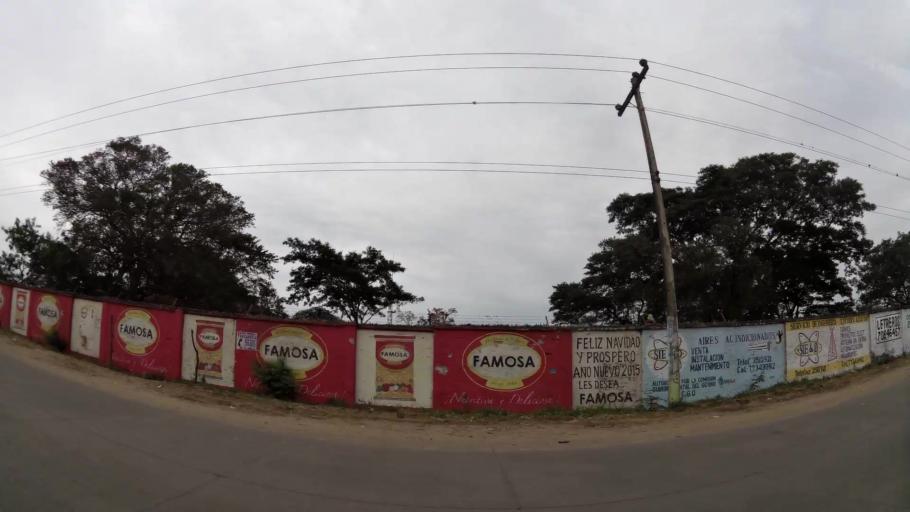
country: BO
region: Santa Cruz
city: Santa Cruz de la Sierra
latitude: -17.8092
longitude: -63.1577
